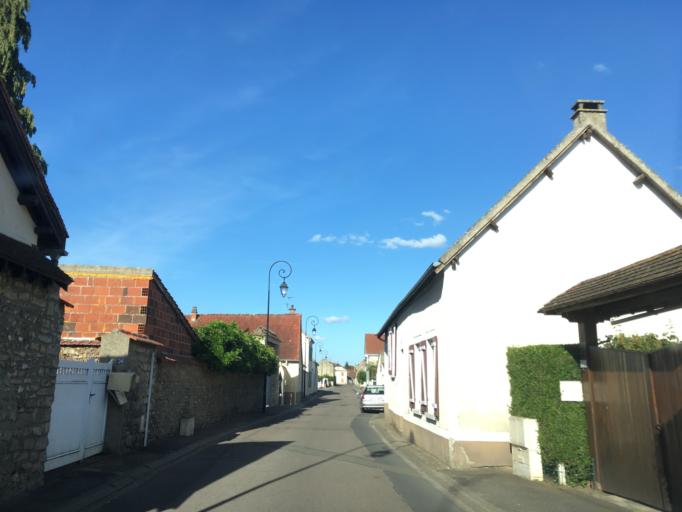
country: FR
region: Haute-Normandie
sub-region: Departement de l'Eure
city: Gasny
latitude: 49.0882
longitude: 1.6006
